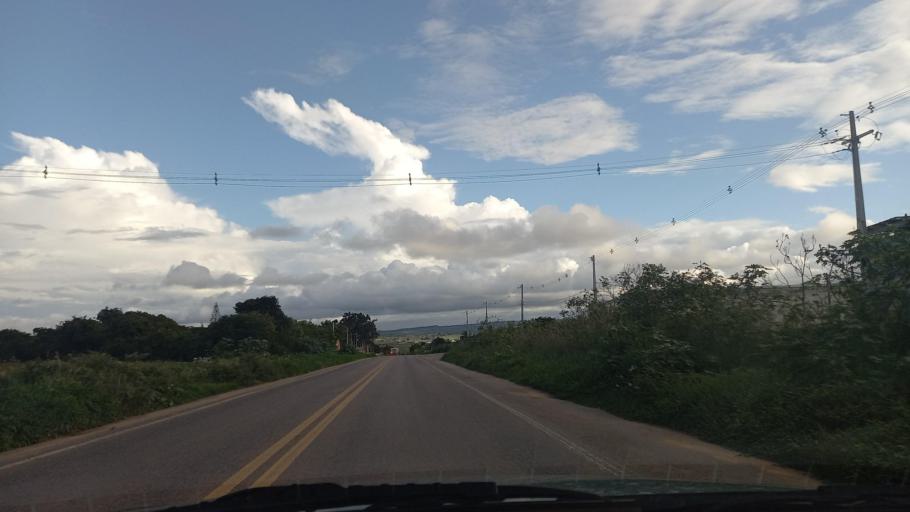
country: BR
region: Pernambuco
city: Garanhuns
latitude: -8.9128
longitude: -36.4882
